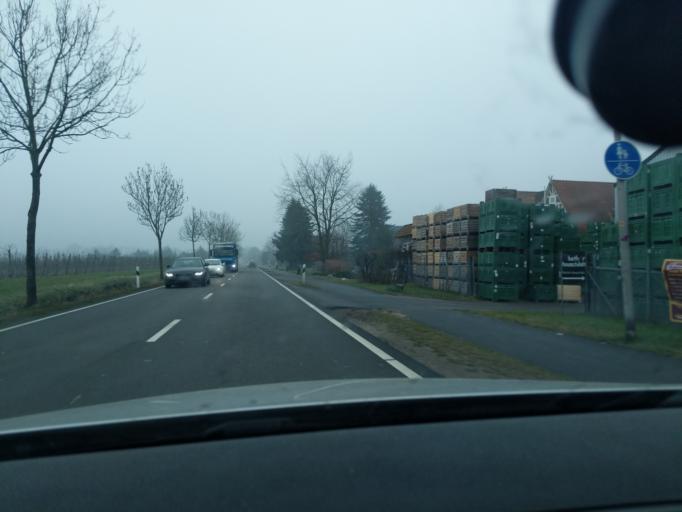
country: DE
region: Lower Saxony
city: Jork
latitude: 53.5424
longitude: 9.6825
